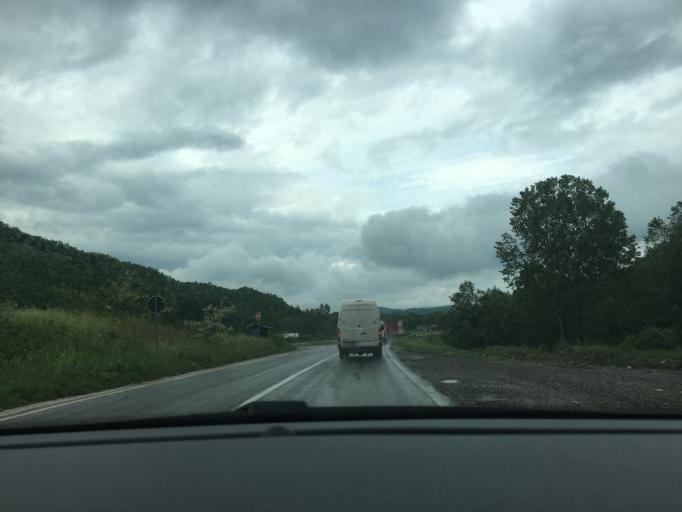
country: MK
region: Debarca
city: Belcista
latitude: 41.3260
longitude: 20.7937
